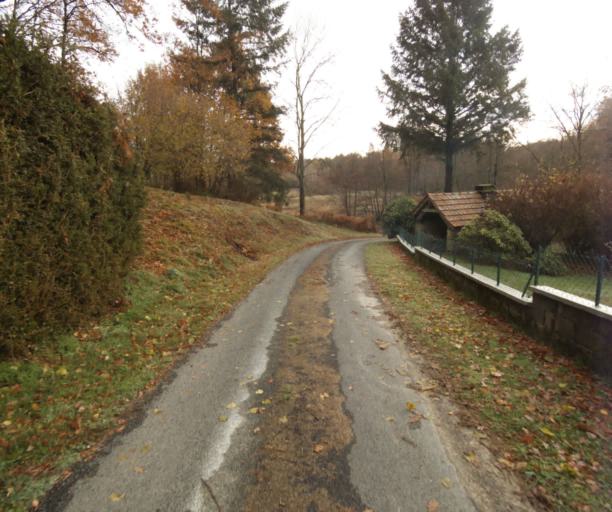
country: FR
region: Limousin
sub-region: Departement de la Correze
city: Cornil
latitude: 45.1969
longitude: 1.7160
